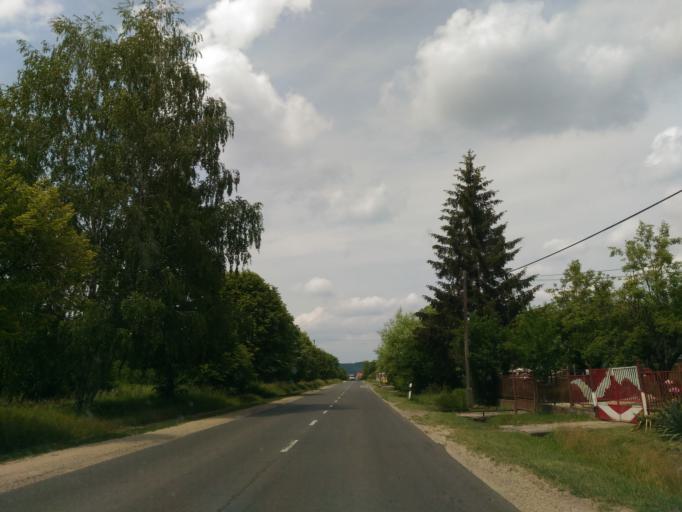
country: HU
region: Baranya
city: Komlo
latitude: 46.2046
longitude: 18.2490
